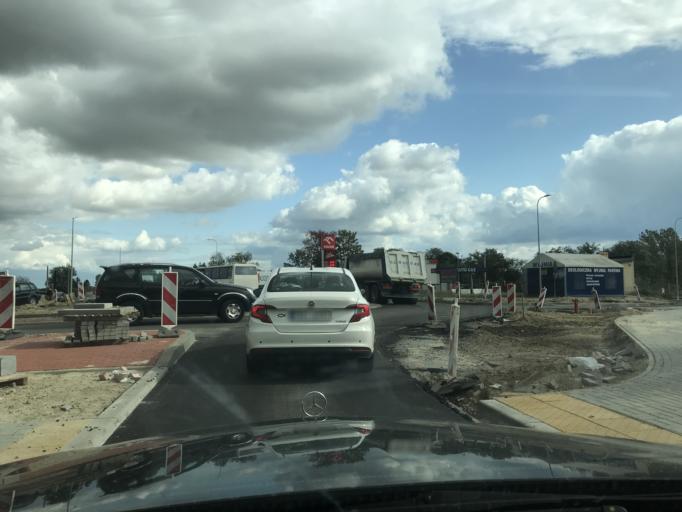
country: PL
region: Lublin Voivodeship
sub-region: Powiat lubartowski
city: Lubartow
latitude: 51.4745
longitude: 22.6042
